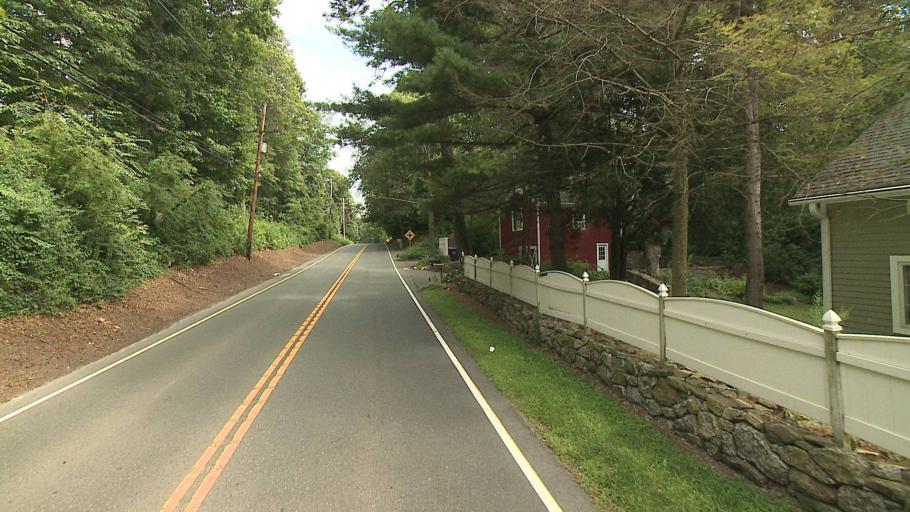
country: US
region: New York
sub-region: Putnam County
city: Putnam Lake
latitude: 41.4739
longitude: -73.4686
